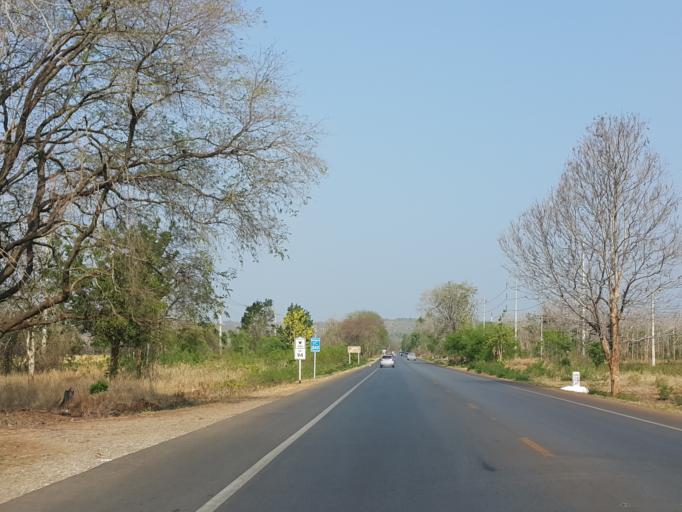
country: TH
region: Kanchanaburi
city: Sai Yok
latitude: 14.0971
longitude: 99.2457
